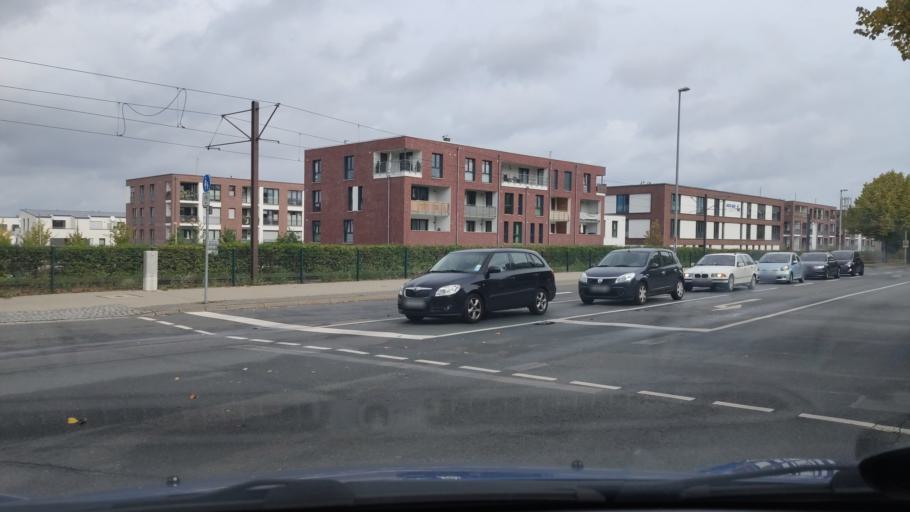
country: DE
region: Lower Saxony
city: Ronnenberg
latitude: 52.3771
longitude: 9.6675
